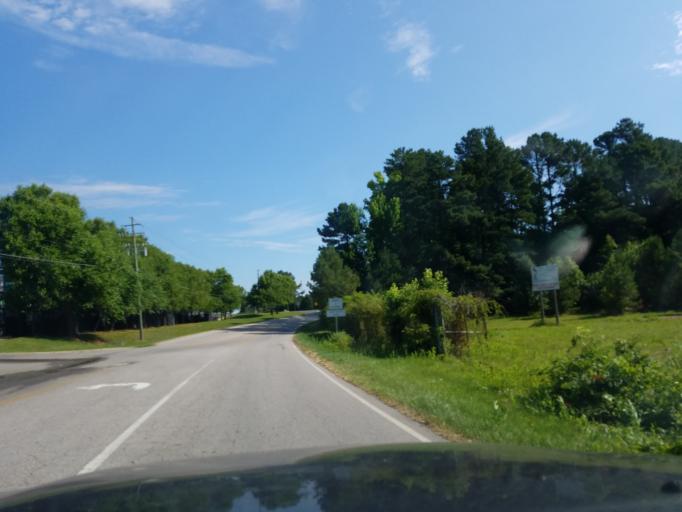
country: US
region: North Carolina
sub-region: Vance County
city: Henderson
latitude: 36.3382
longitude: -78.4379
